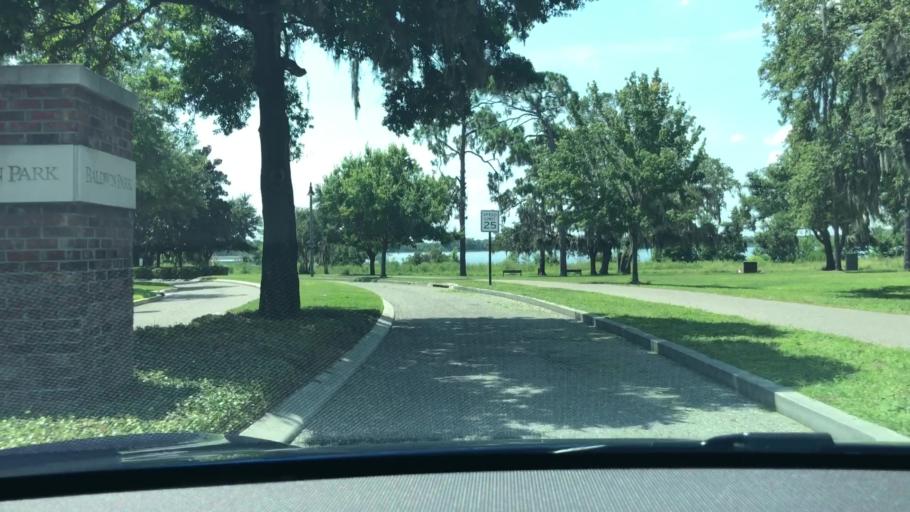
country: US
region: Florida
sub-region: Orange County
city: Winter Park
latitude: 28.5785
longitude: -81.3238
